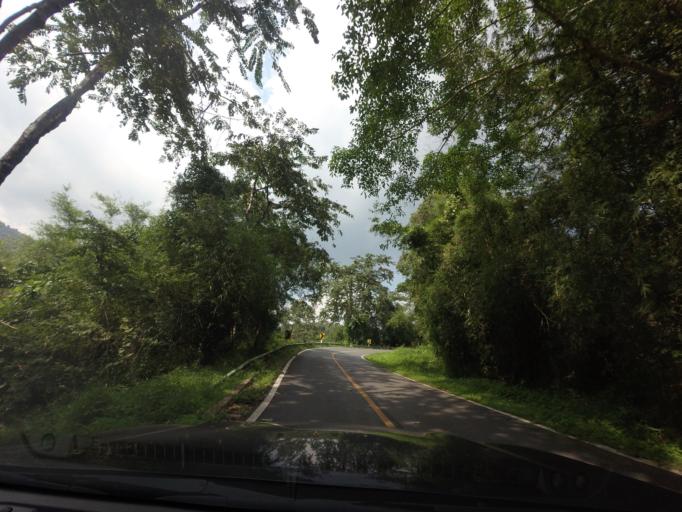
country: TH
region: Nan
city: Bo Kluea
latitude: 19.1621
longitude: 101.1619
